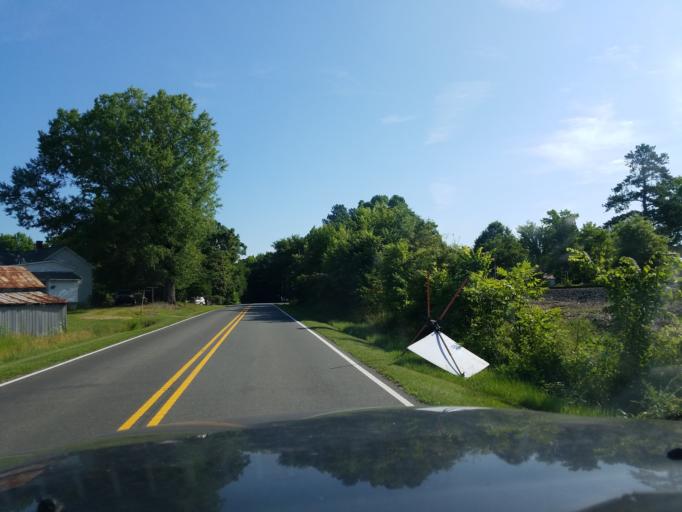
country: US
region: North Carolina
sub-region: Granville County
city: Butner
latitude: 36.1995
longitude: -78.7247
